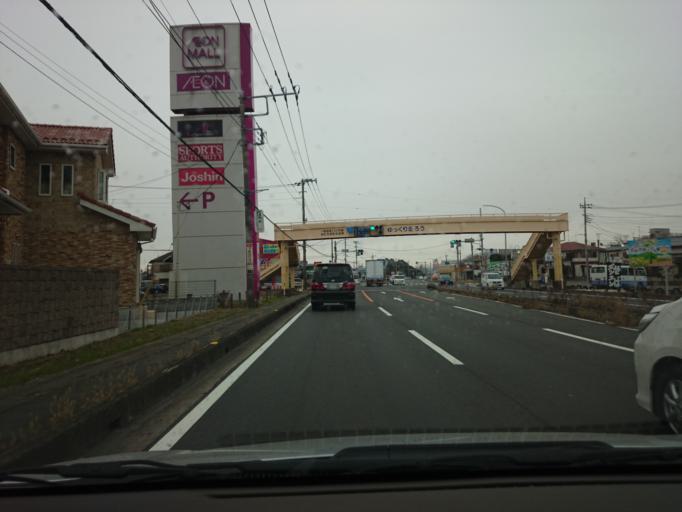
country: JP
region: Saitama
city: Hanyu
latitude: 36.1459
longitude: 139.5436
